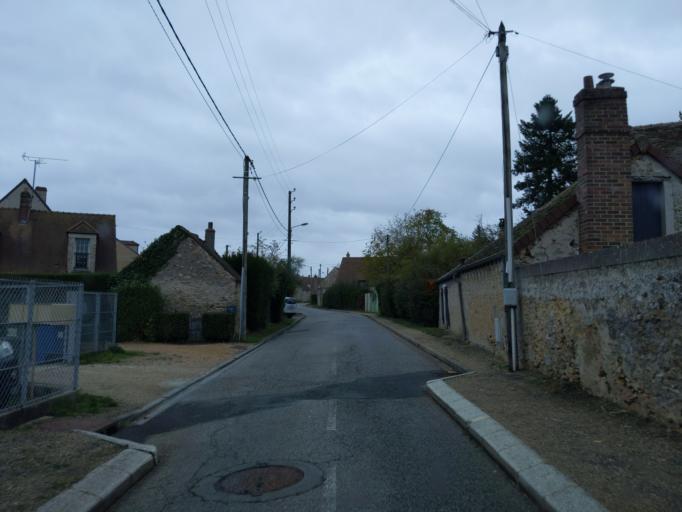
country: FR
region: Ile-de-France
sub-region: Departement des Yvelines
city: Bullion
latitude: 48.6227
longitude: 1.9912
